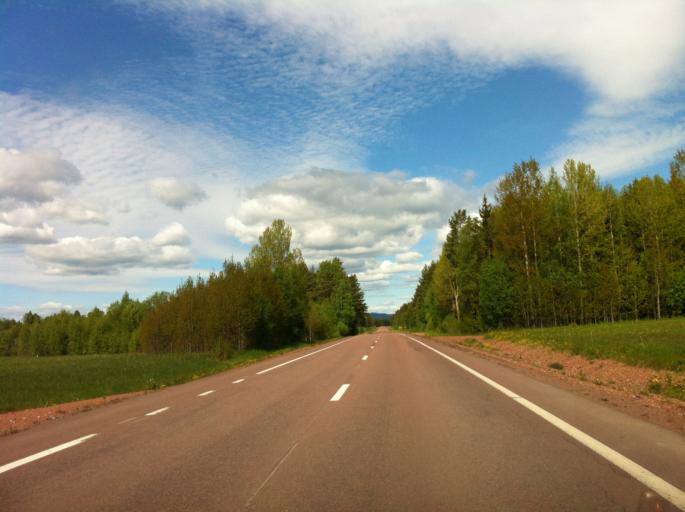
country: SE
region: Dalarna
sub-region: Mora Kommun
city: Mora
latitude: 60.9187
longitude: 14.5960
